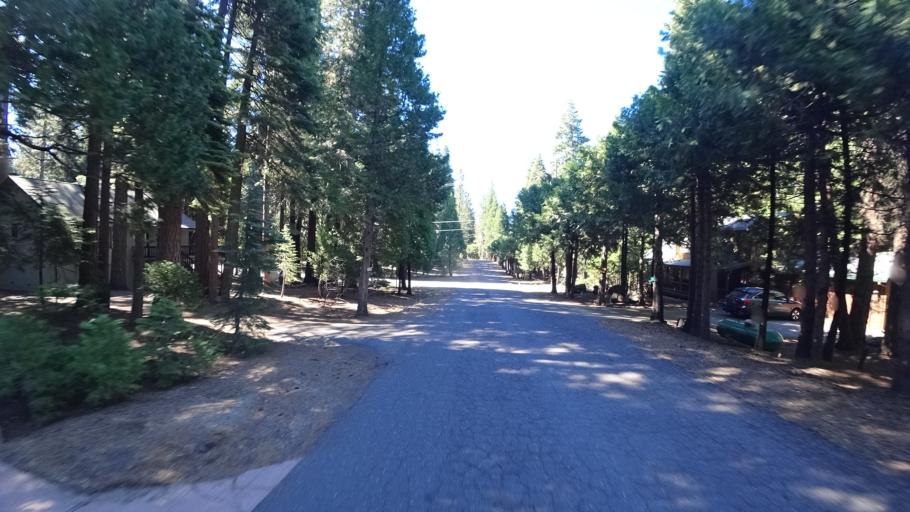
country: US
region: California
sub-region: Calaveras County
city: Arnold
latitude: 38.2977
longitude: -120.2705
